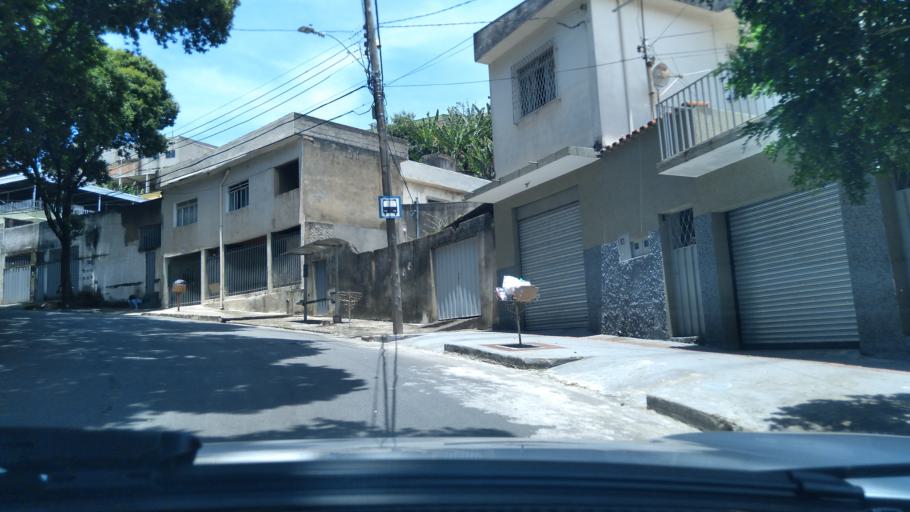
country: BR
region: Minas Gerais
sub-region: Contagem
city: Contagem
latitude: -19.9277
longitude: -44.0128
